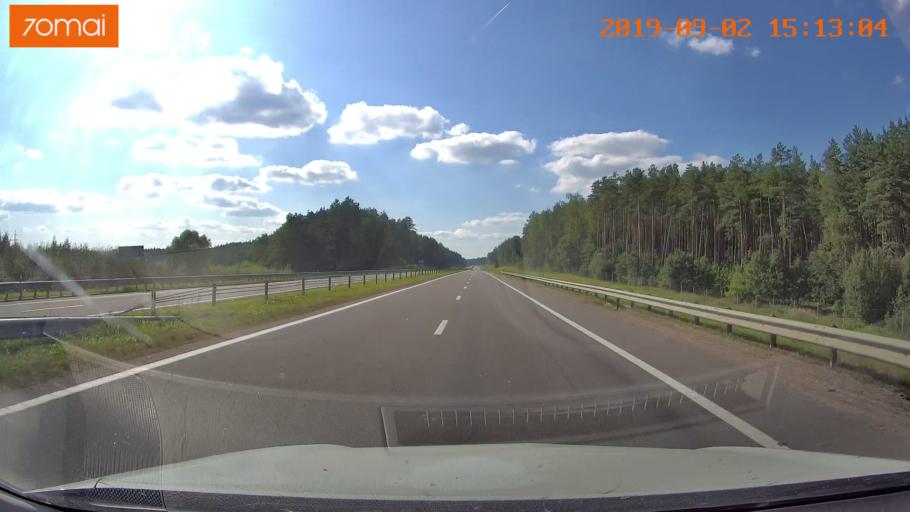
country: BY
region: Mogilev
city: Byalynichy
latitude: 53.9670
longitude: 29.7109
